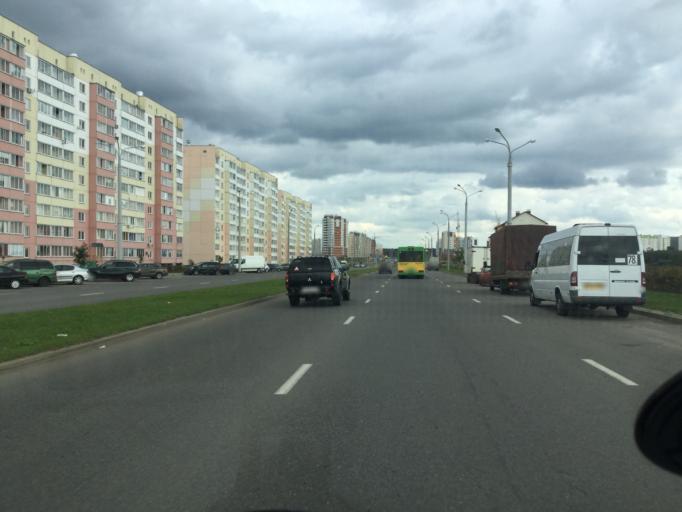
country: BY
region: Vitebsk
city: Vitebsk
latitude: 55.1660
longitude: 30.2572
